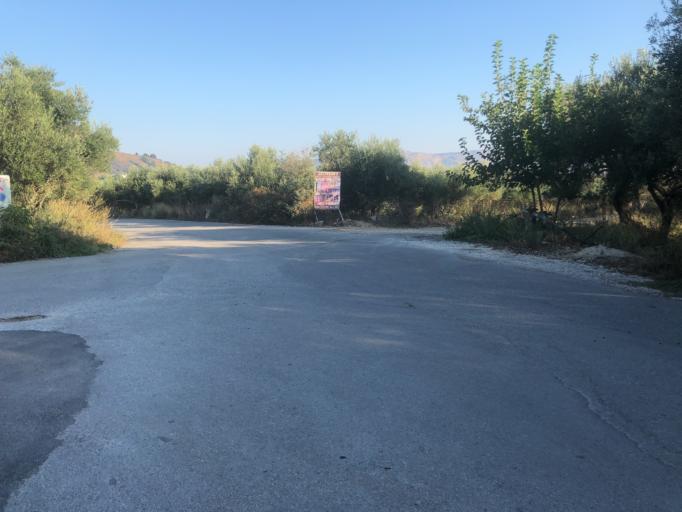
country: GR
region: Crete
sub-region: Nomos Chanias
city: Georgioupolis
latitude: 35.3383
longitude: 24.2857
